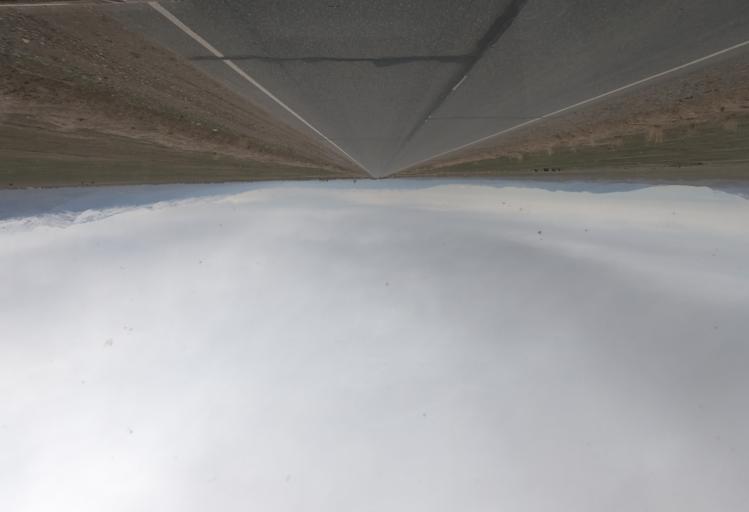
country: KG
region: Naryn
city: At-Bashi
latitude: 41.0688
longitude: 75.5262
